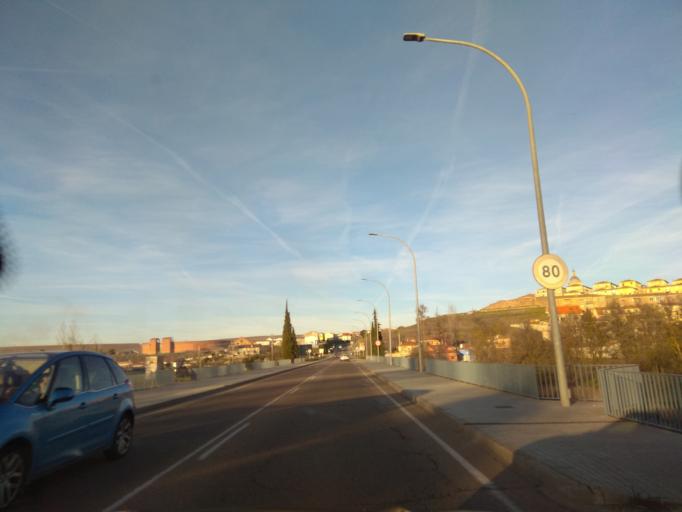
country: ES
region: Castille and Leon
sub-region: Provincia de Salamanca
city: Ciudad Rodrigo
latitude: 40.5954
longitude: -6.5409
